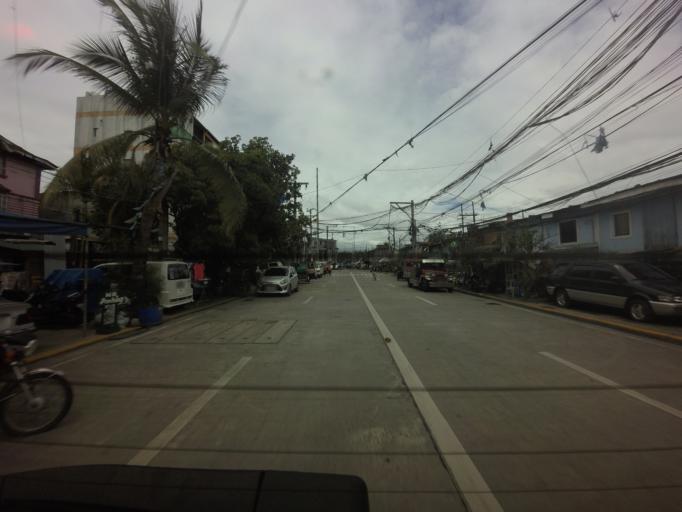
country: PH
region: Metro Manila
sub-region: City of Manila
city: Manila
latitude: 14.6193
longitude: 120.9742
